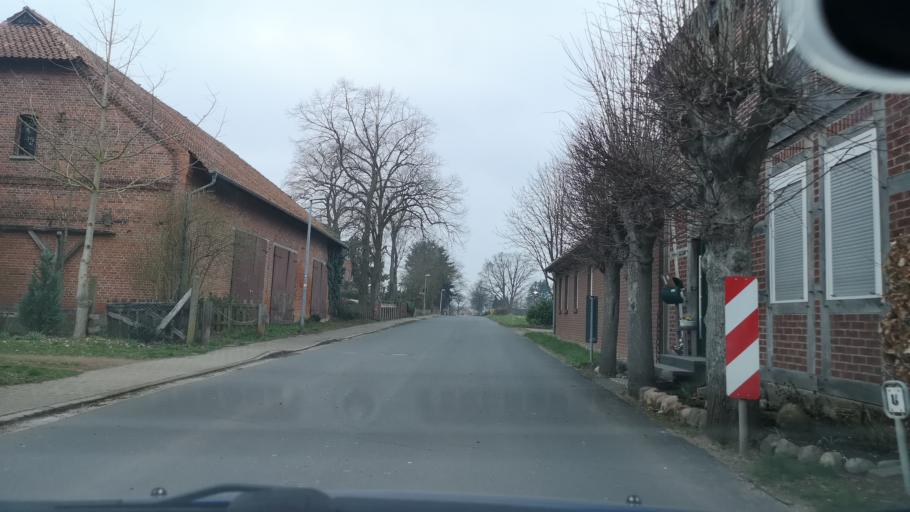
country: DE
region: Lower Saxony
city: Schwarmstedt
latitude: 52.5955
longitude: 9.5672
